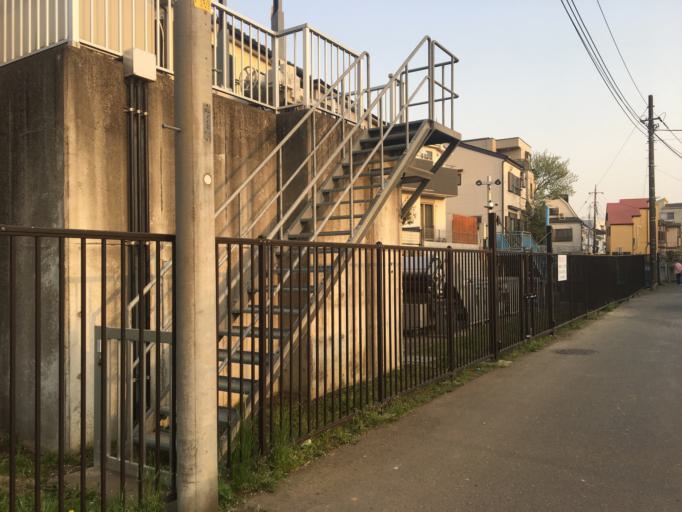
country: JP
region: Saitama
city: Shiki
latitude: 35.8331
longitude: 139.5679
